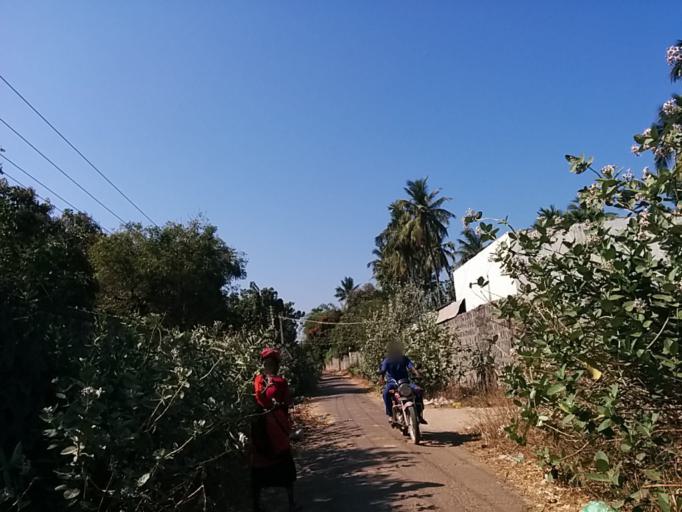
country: IN
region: Pondicherry
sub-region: Puducherry
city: Puducherry
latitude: 11.9641
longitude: 79.8253
